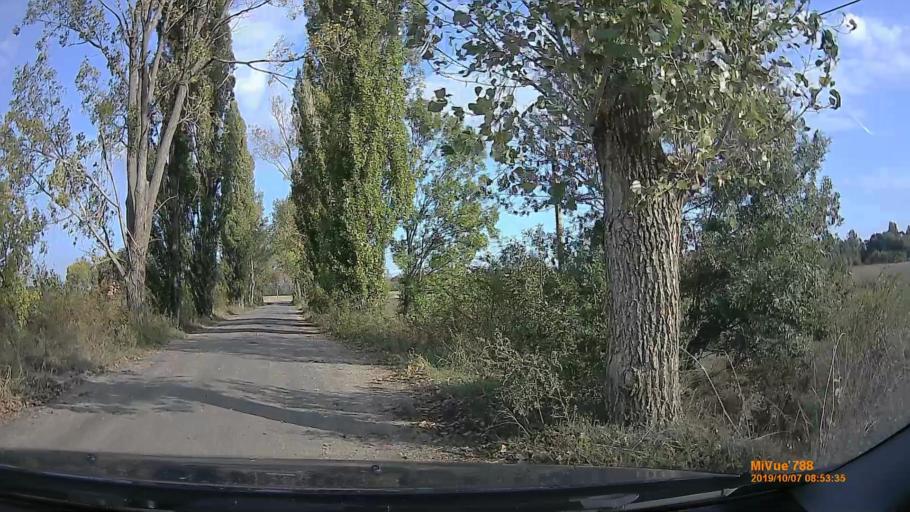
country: HU
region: Bekes
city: Szarvas
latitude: 46.8190
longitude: 20.5252
